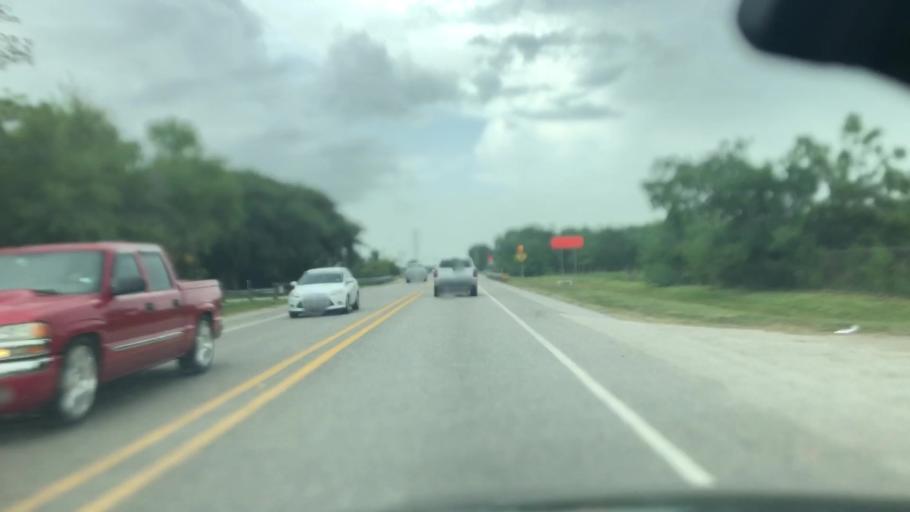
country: US
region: Texas
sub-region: Galveston County
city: Dickinson
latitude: 29.4862
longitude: -95.0618
